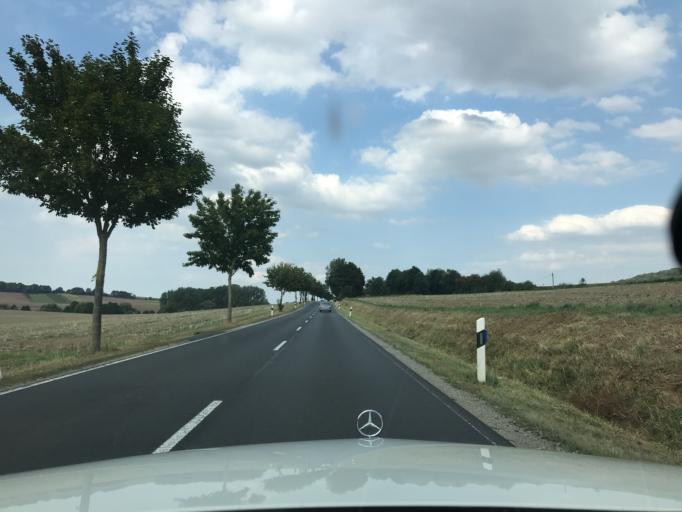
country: DE
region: Lower Saxony
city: Adelebsen
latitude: 51.5899
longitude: 9.7668
